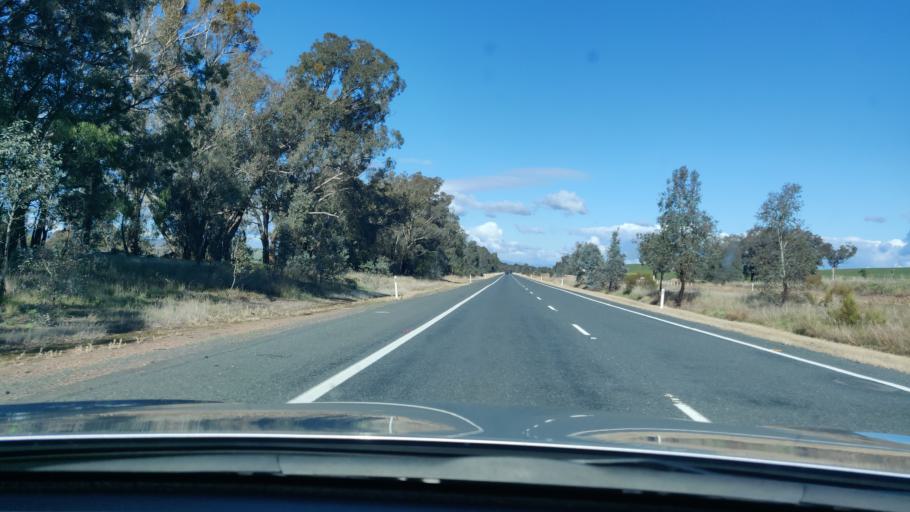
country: AU
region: New South Wales
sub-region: Greater Hume Shire
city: Holbrook
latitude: -35.5587
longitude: 147.5351
